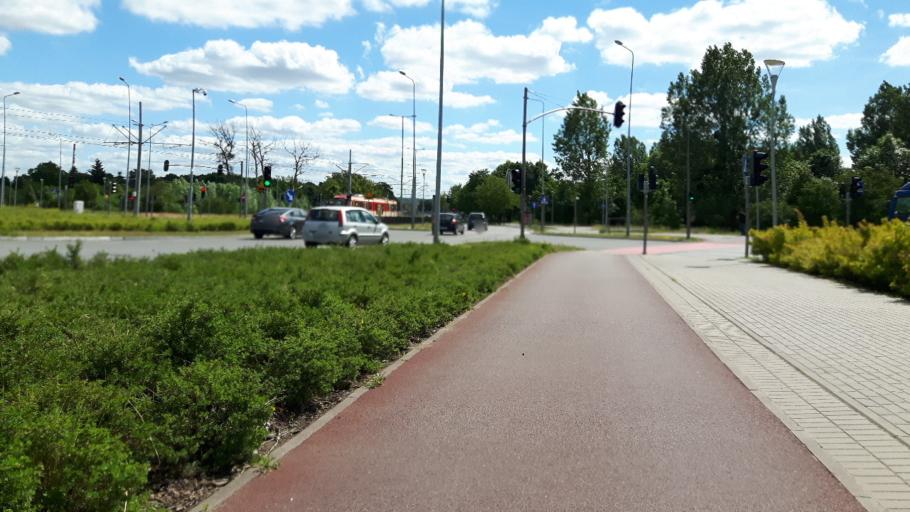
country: PL
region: Pomeranian Voivodeship
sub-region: Gdansk
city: Gdansk
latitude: 54.4024
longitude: 18.6223
